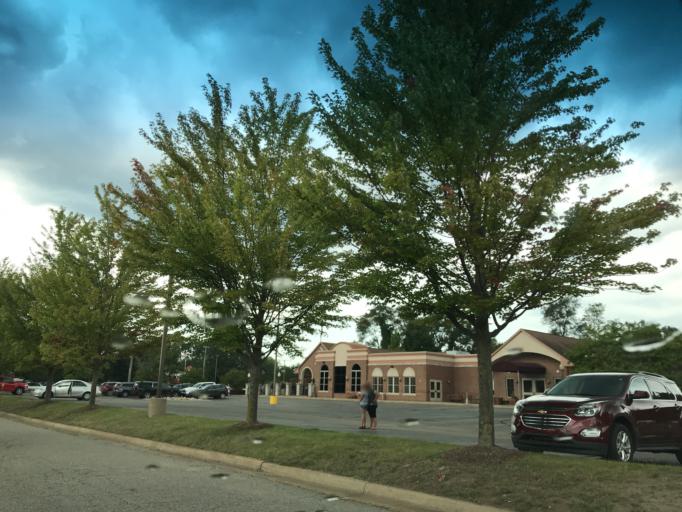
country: US
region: Michigan
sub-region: Oakland County
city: Milford
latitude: 42.5590
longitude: -83.6167
